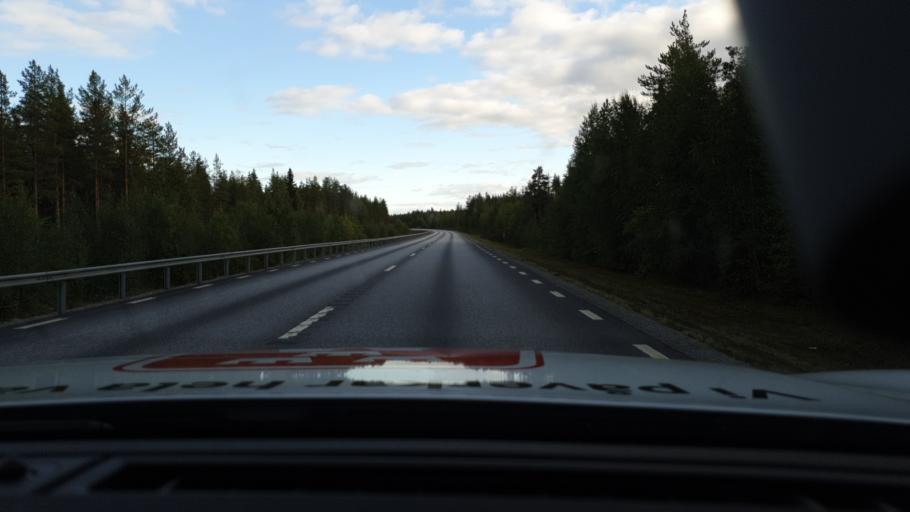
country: SE
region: Norrbotten
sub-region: Overkalix Kommun
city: OEverkalix
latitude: 66.6381
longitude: 22.2012
